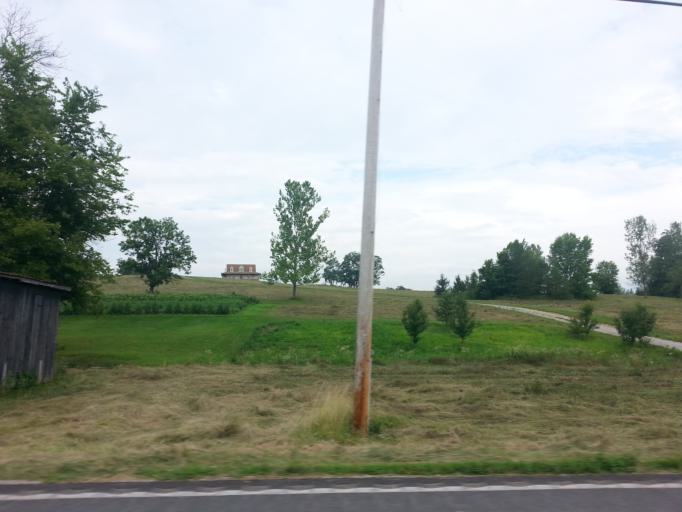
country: US
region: Kentucky
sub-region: Harrison County
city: Cynthiana
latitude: 38.4524
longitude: -84.2402
